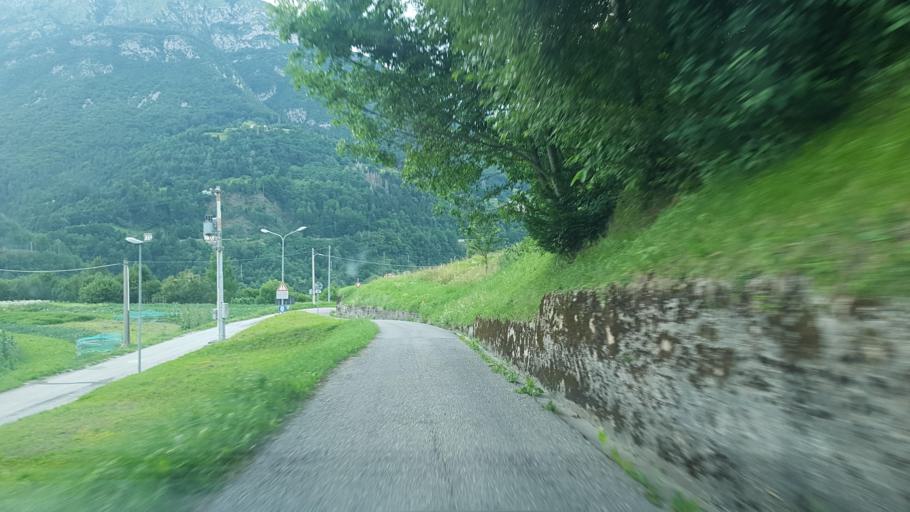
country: IT
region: Friuli Venezia Giulia
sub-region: Provincia di Udine
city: Paularo
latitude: 46.4812
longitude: 13.0983
